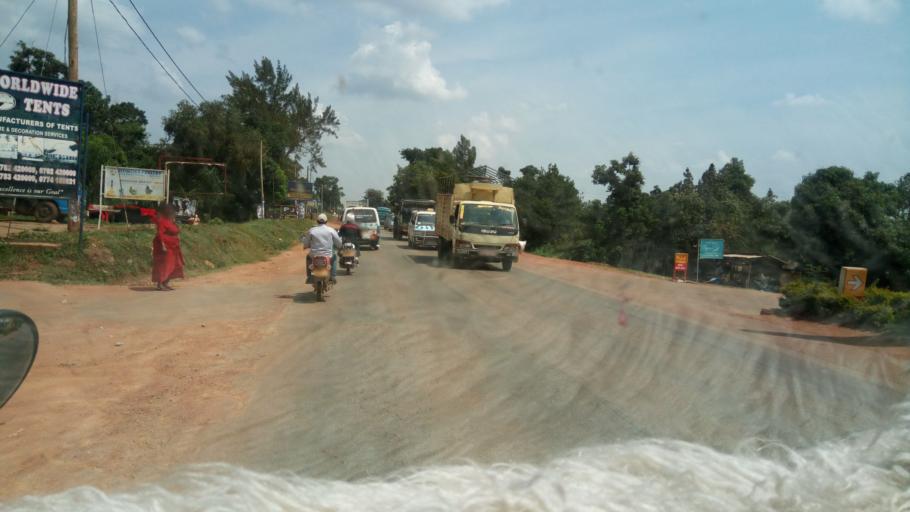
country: UG
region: Central Region
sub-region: Mukono District
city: Mukono
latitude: 0.3690
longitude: 32.7375
